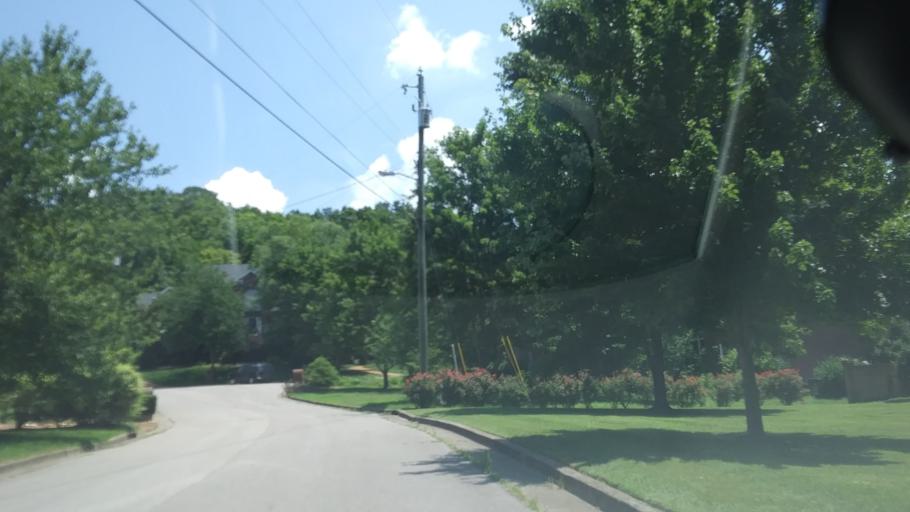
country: US
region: Tennessee
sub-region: Davidson County
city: Belle Meade
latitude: 36.0892
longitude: -86.9436
